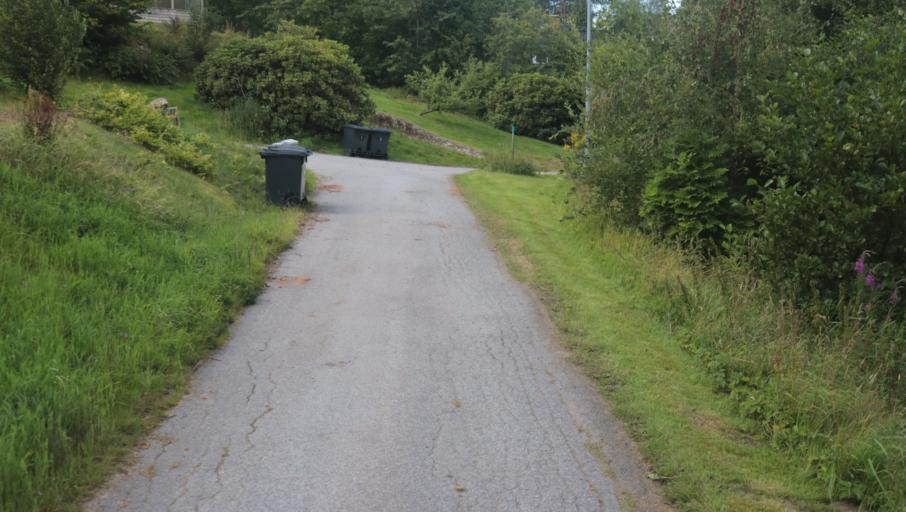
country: SE
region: Blekinge
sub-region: Karlshamns Kommun
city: Svangsta
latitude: 56.2573
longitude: 14.7713
